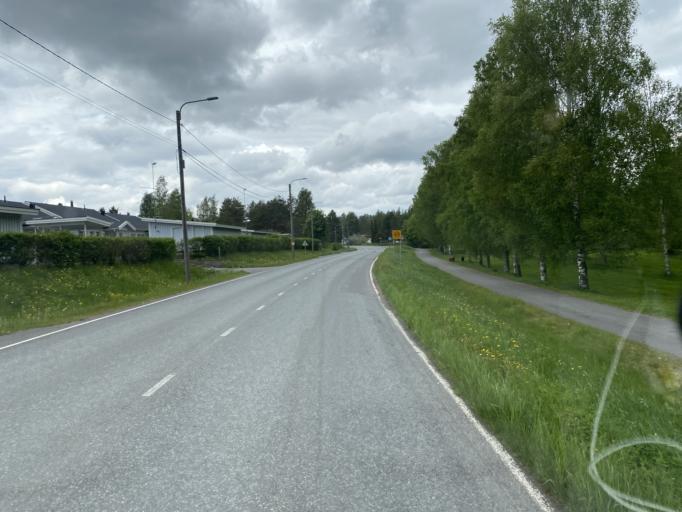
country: FI
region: Pirkanmaa
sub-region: Etelae-Pirkanmaa
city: Urjala
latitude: 61.0778
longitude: 23.5654
